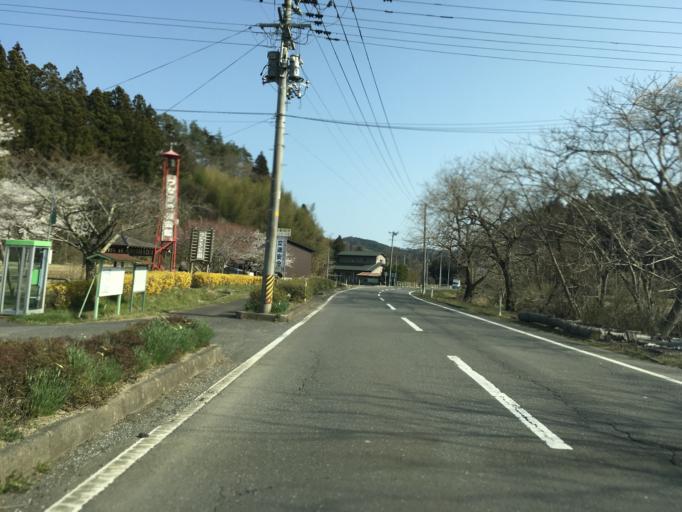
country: JP
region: Iwate
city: Ichinoseki
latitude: 38.7855
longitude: 141.3249
